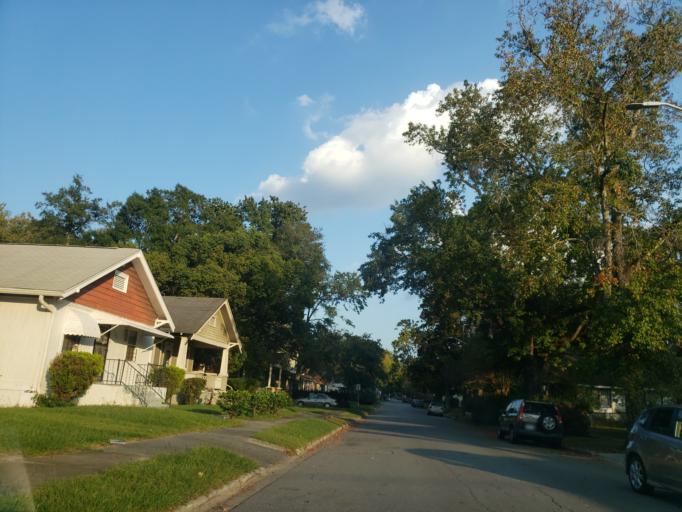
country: US
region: Georgia
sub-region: Chatham County
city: Savannah
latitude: 32.0569
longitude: -81.0863
